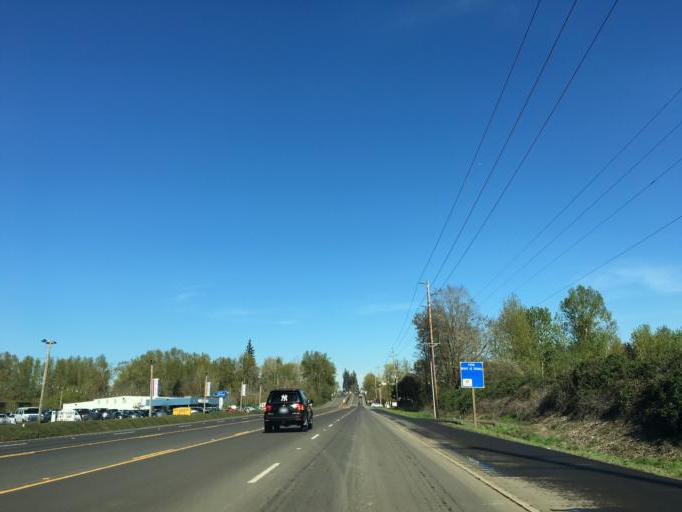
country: US
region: Oregon
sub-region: Clackamas County
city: Canby
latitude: 45.2542
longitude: -122.7127
